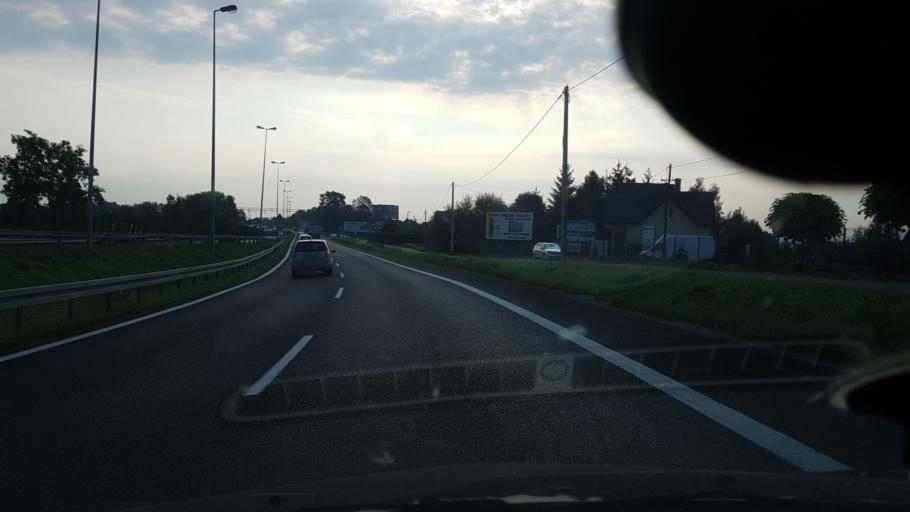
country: PL
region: Lesser Poland Voivodeship
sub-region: Powiat myslenicki
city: Beczarka
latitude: 49.8787
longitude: 19.8804
